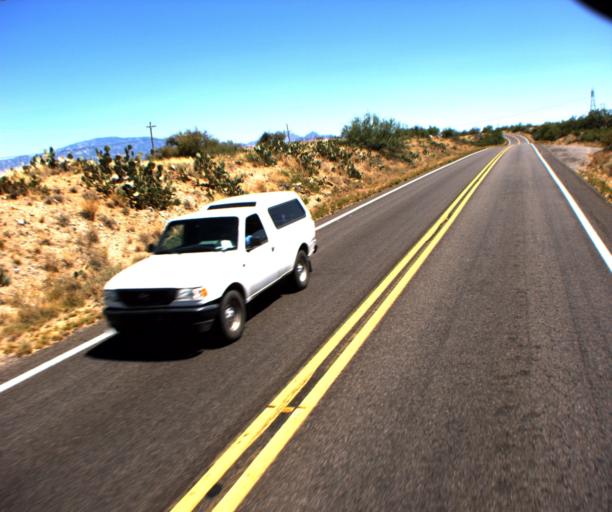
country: US
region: Arizona
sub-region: Pima County
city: Catalina
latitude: 32.6118
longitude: -110.9871
